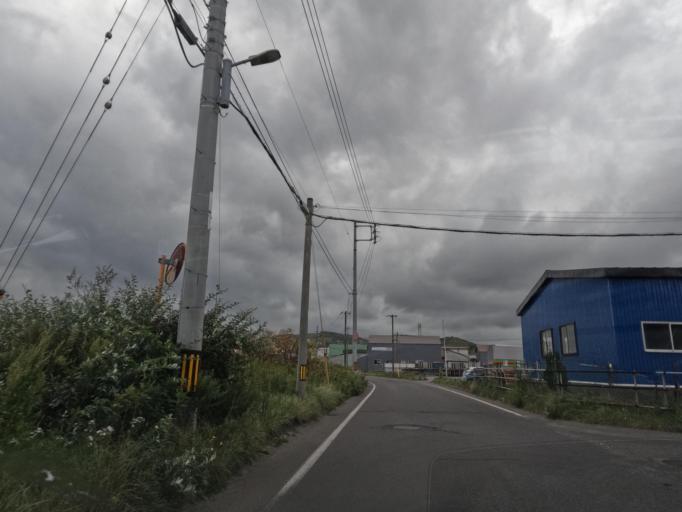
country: JP
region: Hokkaido
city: Muroran
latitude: 42.3381
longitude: 141.0284
